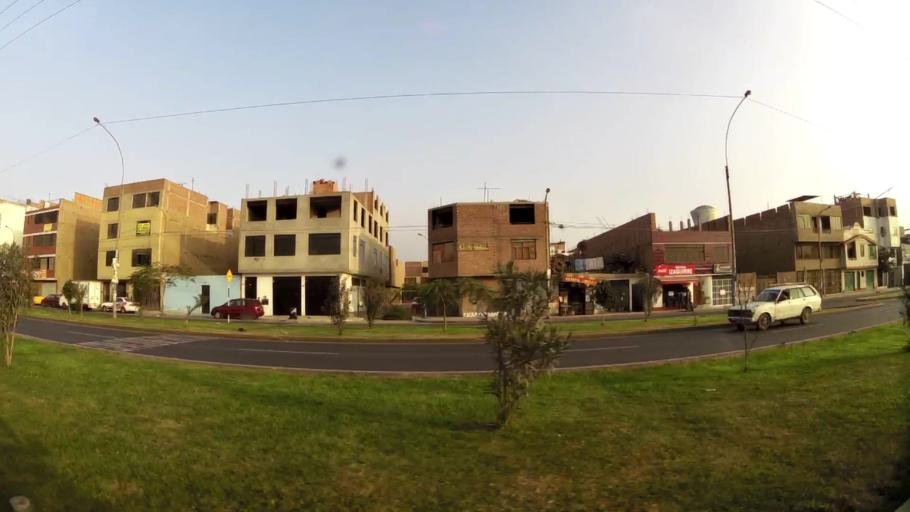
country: PE
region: Lima
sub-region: Lima
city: Independencia
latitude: -11.9911
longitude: -77.0899
